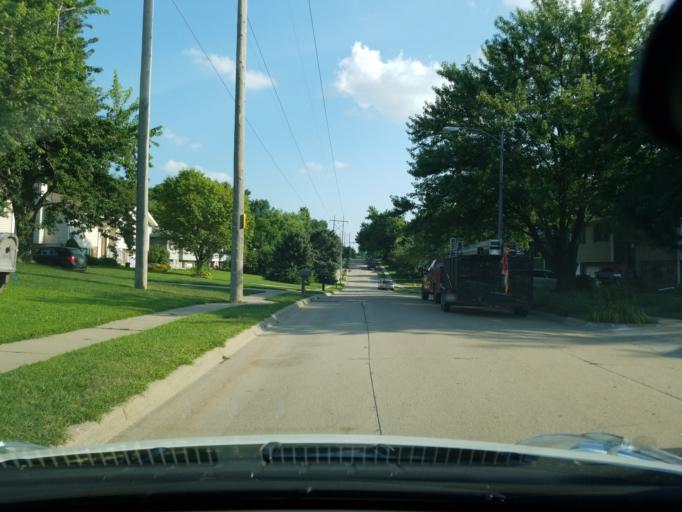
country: US
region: Nebraska
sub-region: Sarpy County
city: Offutt Air Force Base
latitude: 41.1319
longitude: -95.9619
